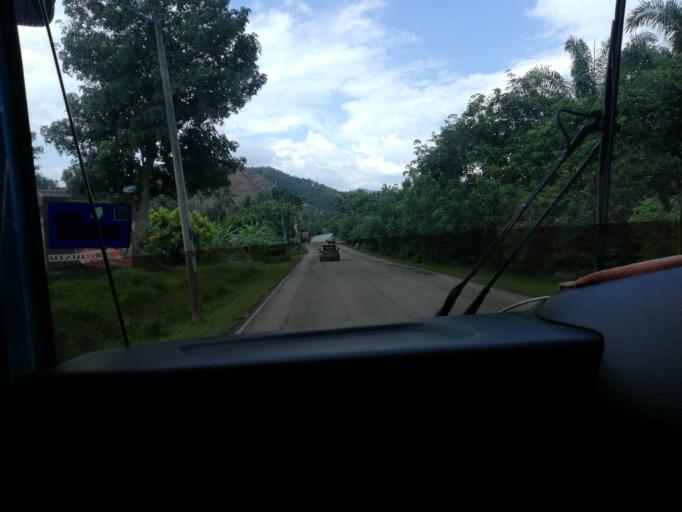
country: MY
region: Kedah
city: Kulim
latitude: 5.2691
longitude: 100.6136
